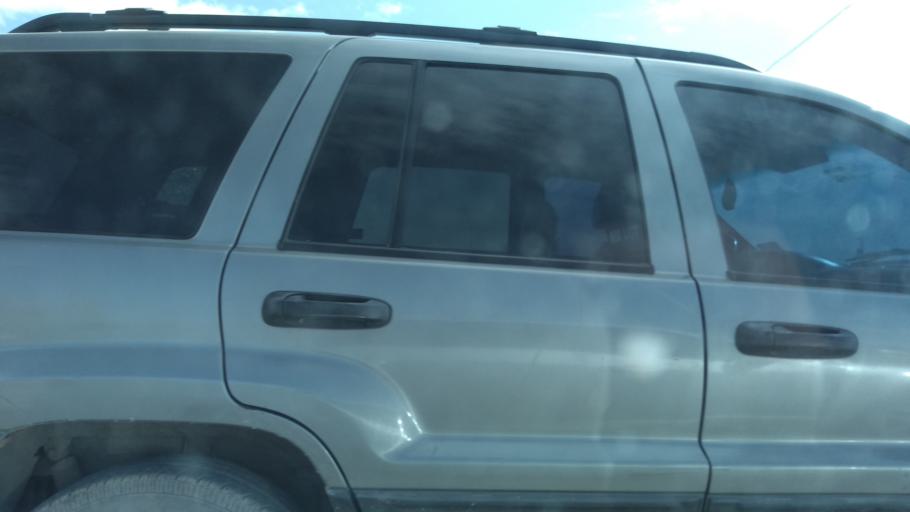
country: US
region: Texas
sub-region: El Paso County
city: San Elizario
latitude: 31.5701
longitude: -106.3418
